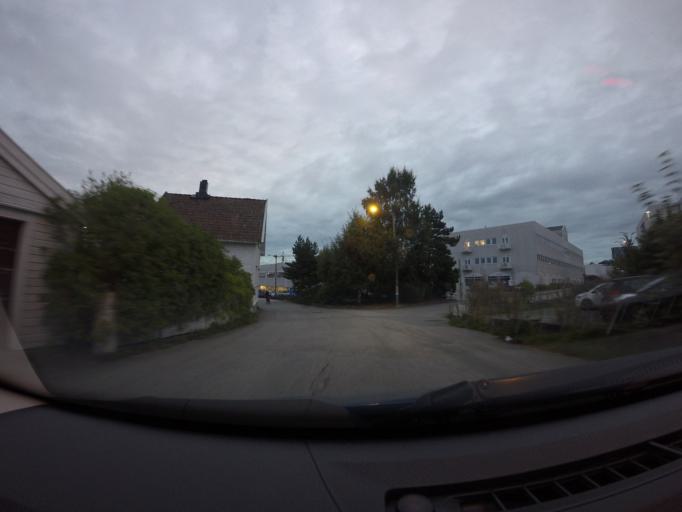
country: NO
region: Rogaland
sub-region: Stavanger
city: Stavanger
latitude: 58.9498
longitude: 5.7380
